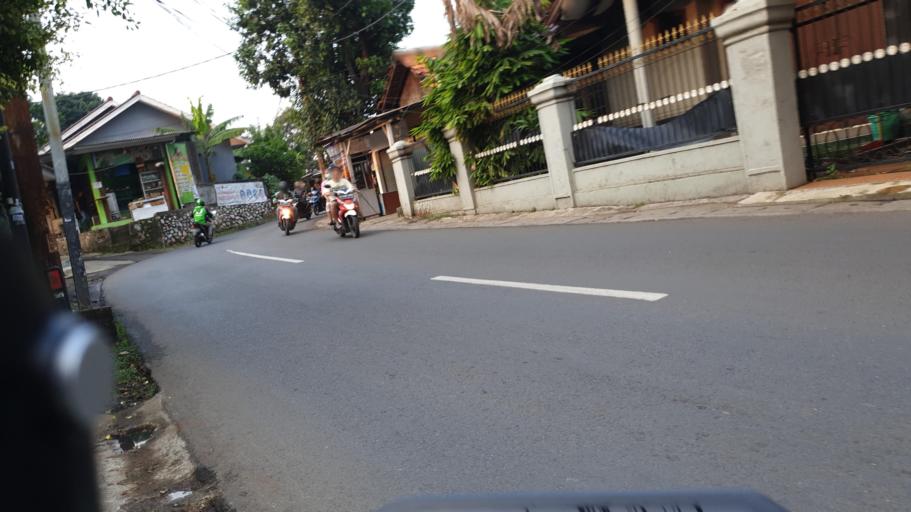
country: ID
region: West Java
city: Depok
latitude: -6.3305
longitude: 106.8288
